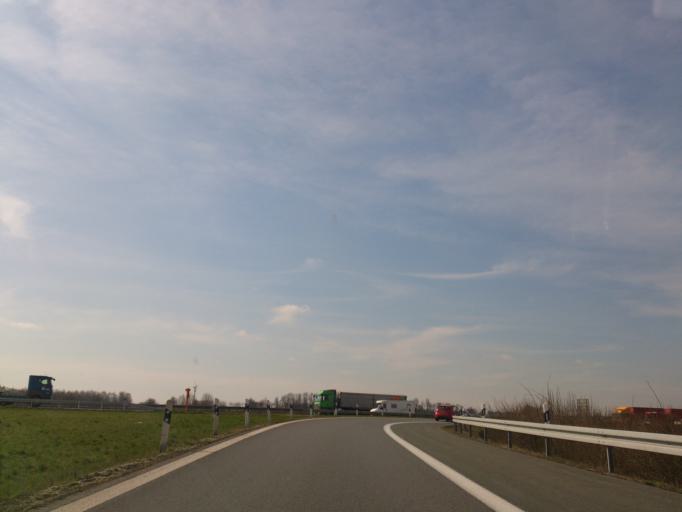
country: DE
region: North Rhine-Westphalia
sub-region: Regierungsbezirk Detmold
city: Buren
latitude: 51.5980
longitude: 8.5829
